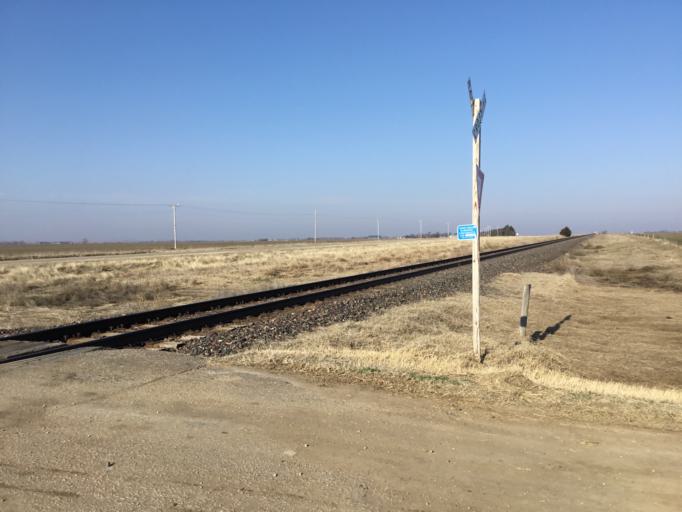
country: US
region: Kansas
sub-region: Ellsworth County
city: Ellsworth
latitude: 38.8269
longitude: -98.4851
